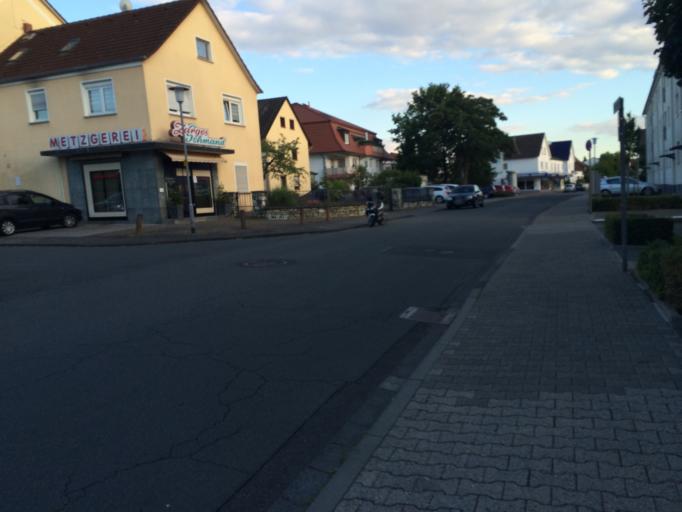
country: DE
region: Hesse
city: Morfelden-Walldorf
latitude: 50.0096
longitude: 8.5794
